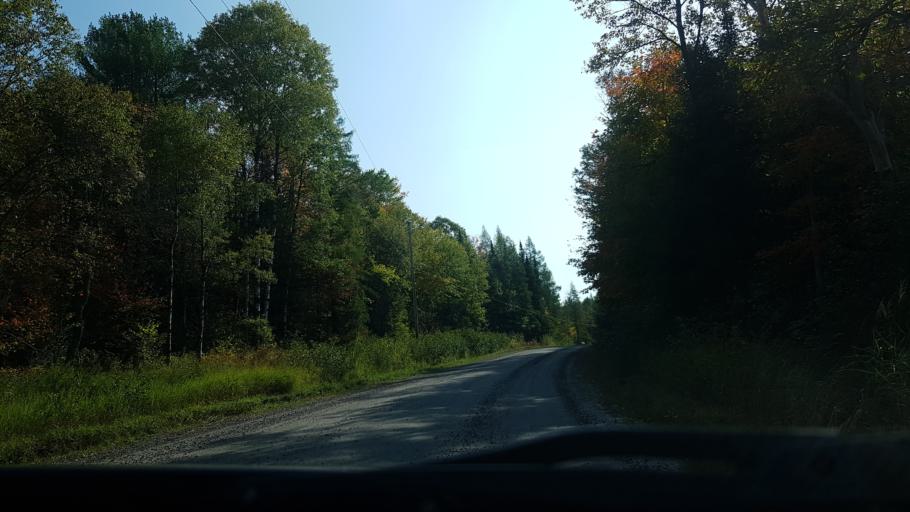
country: CA
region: Ontario
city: Bracebridge
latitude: 44.9400
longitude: -79.2406
